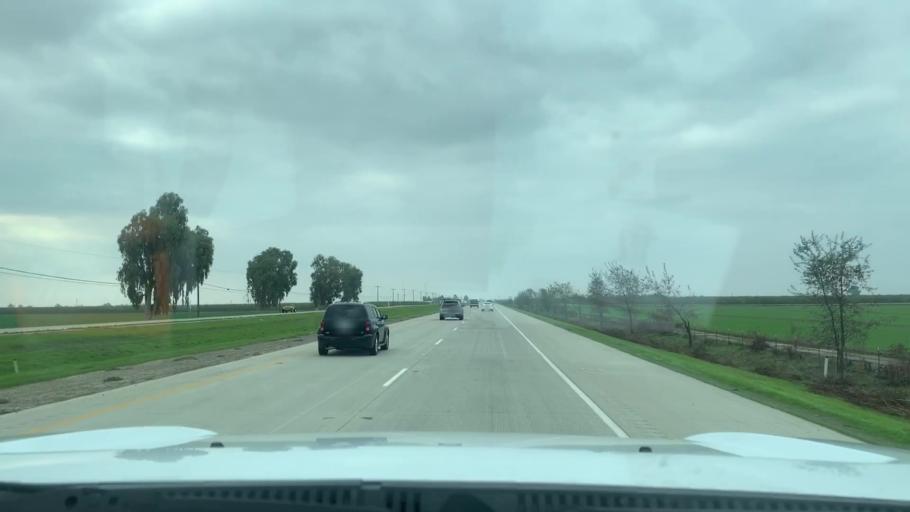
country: US
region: California
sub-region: Kings County
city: Home Garden
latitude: 36.3286
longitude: -119.5386
